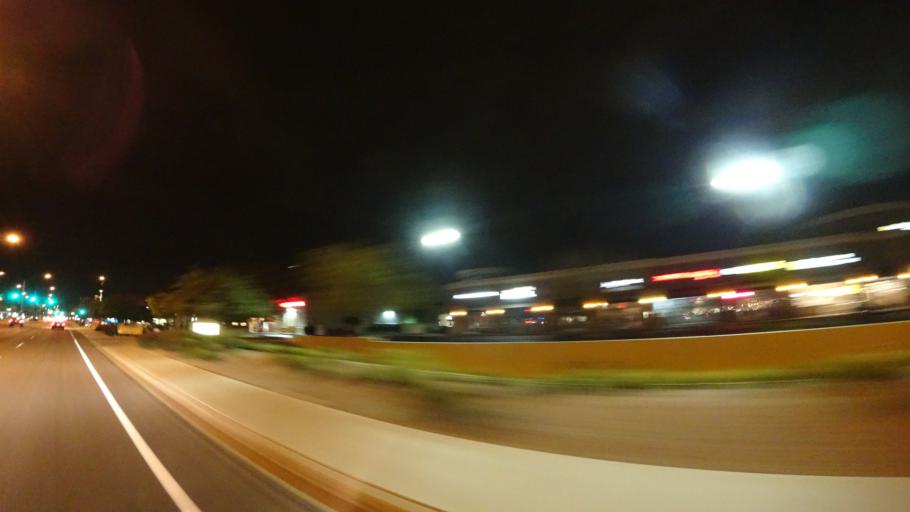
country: US
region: Arizona
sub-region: Maricopa County
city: Gilbert
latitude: 33.3791
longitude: -111.7577
